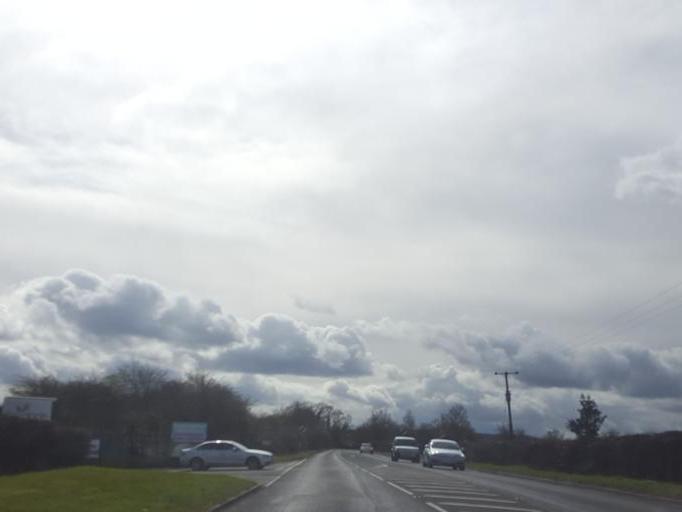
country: GB
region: England
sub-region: Worcestershire
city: Bransford
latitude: 52.1693
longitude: -2.3017
